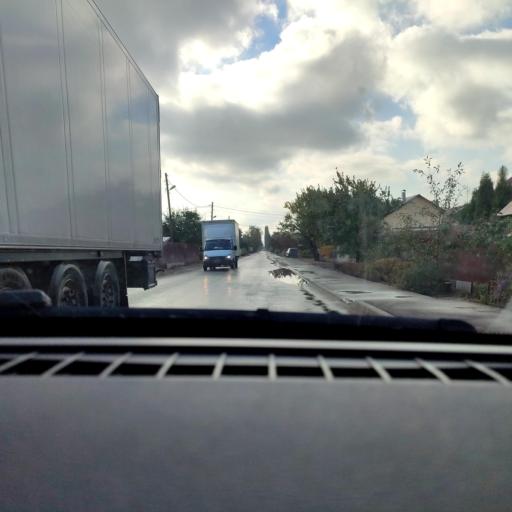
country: RU
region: Voronezj
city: Maslovka
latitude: 51.6095
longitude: 39.2206
